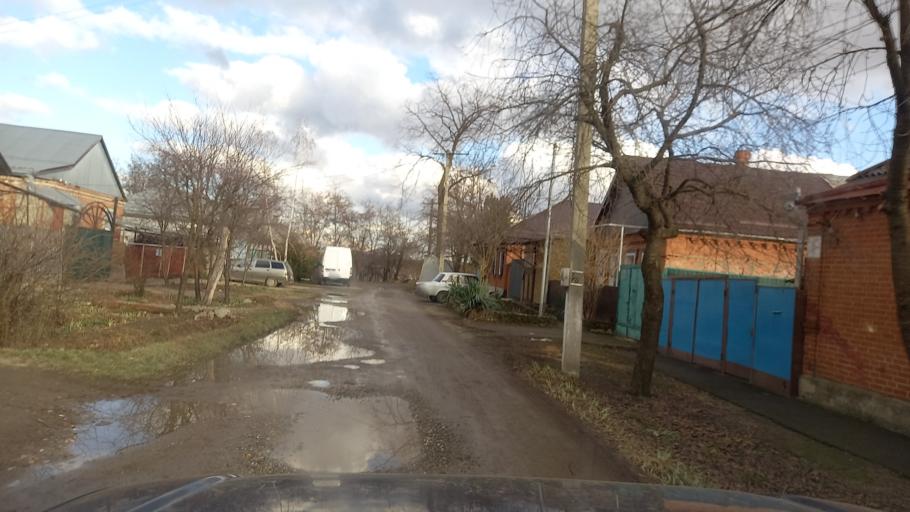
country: RU
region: Adygeya
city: Maykop
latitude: 44.5987
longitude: 40.0800
